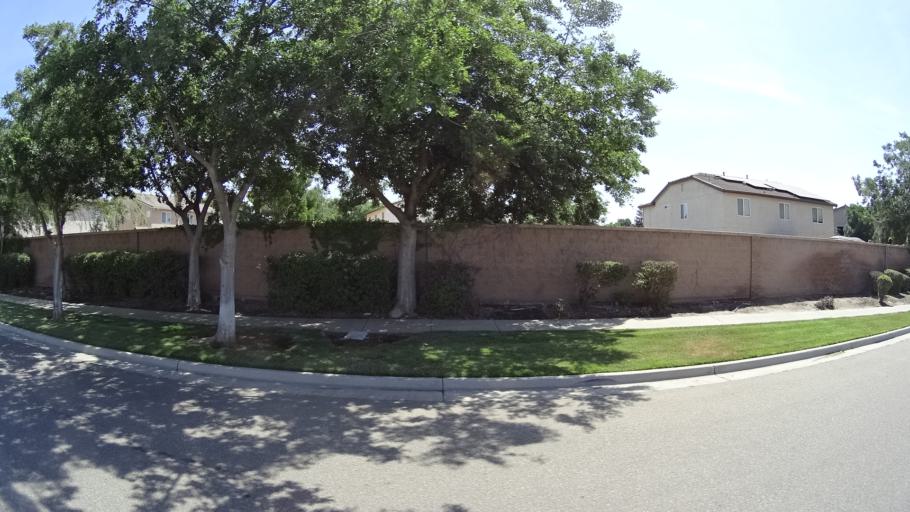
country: US
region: California
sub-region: Kings County
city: Armona
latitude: 36.3448
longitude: -119.6820
